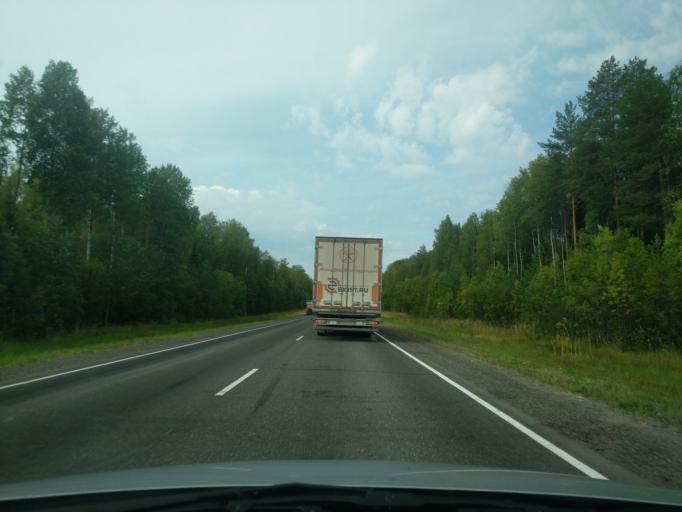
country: RU
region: Kirov
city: Leninskoye
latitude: 58.3191
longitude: 46.8562
